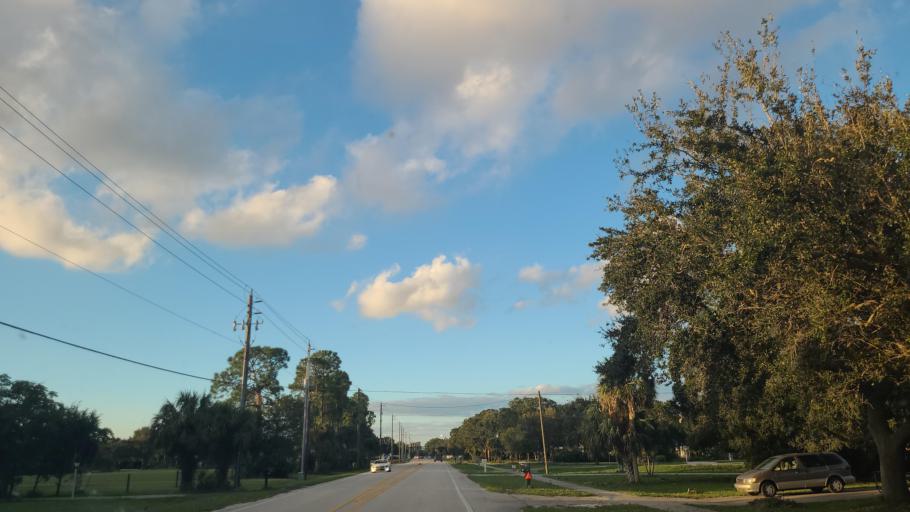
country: US
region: Florida
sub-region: Indian River County
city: Vero Beach South
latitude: 27.6126
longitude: -80.4058
